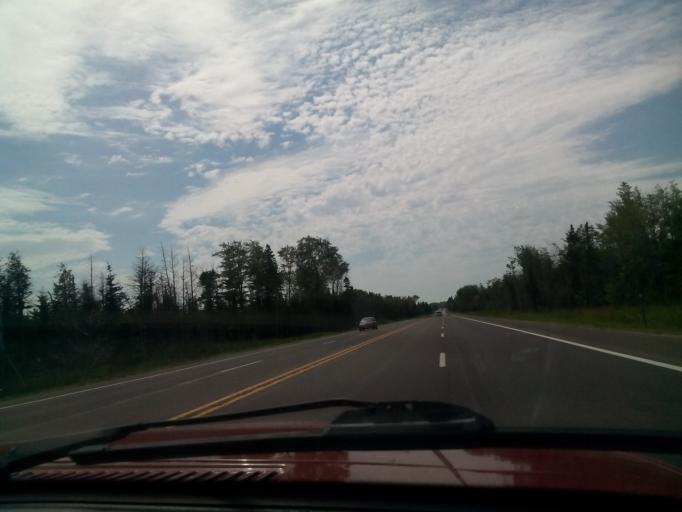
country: US
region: Michigan
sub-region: Schoolcraft County
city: Manistique
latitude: 46.0075
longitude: -85.9976
